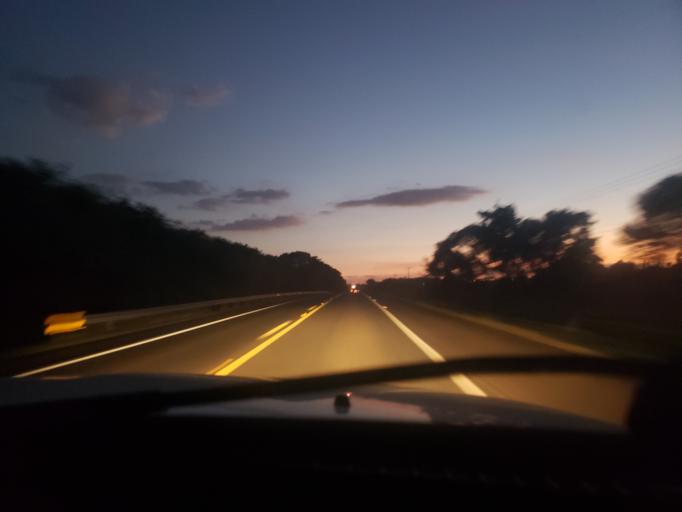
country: BR
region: Sao Paulo
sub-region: Conchal
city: Conchal
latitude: -22.3203
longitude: -47.1391
